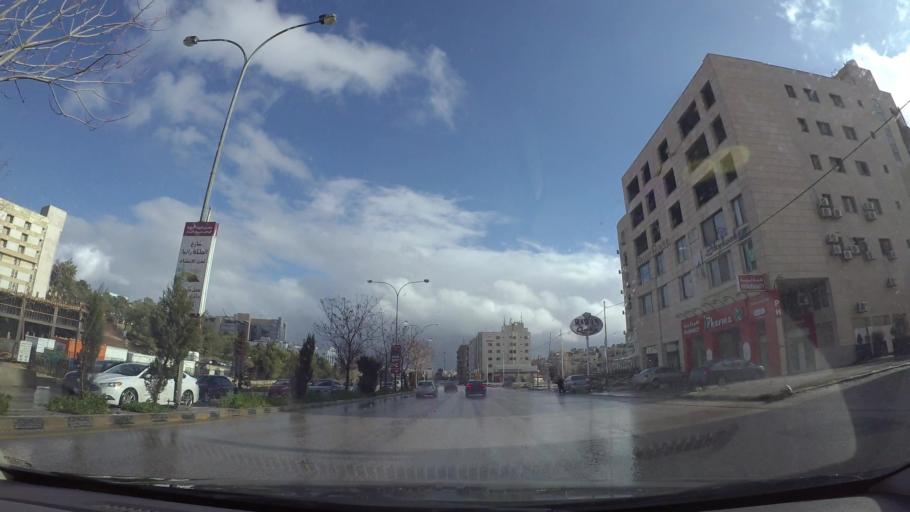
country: JO
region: Amman
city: Al Jubayhah
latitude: 32.0070
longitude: 35.8722
